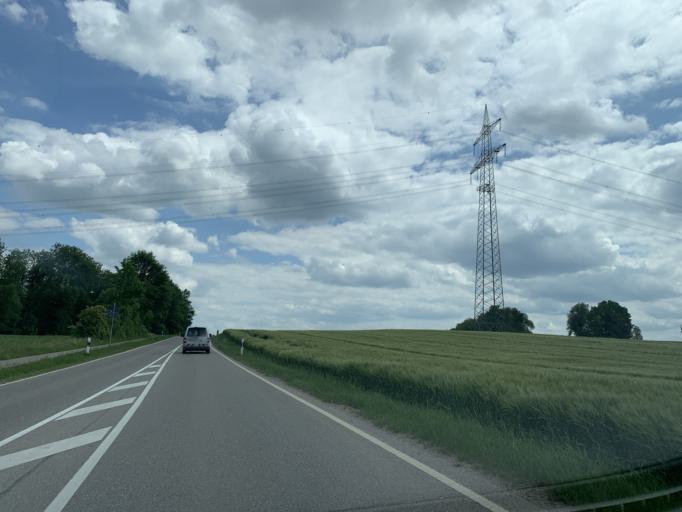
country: DE
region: Bavaria
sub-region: Swabia
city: Senden
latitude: 48.3282
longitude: 10.0120
